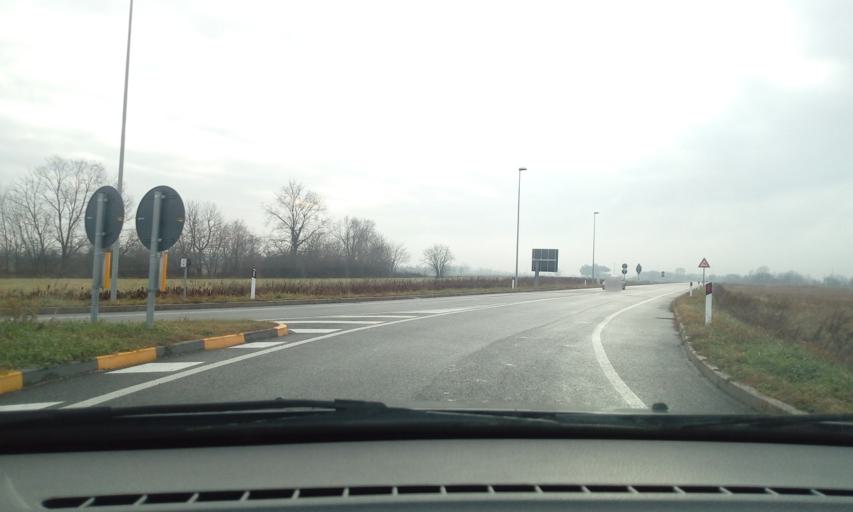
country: IT
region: Friuli Venezia Giulia
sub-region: Provincia di Gorizia
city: Mossa
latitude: 45.9294
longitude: 13.5536
